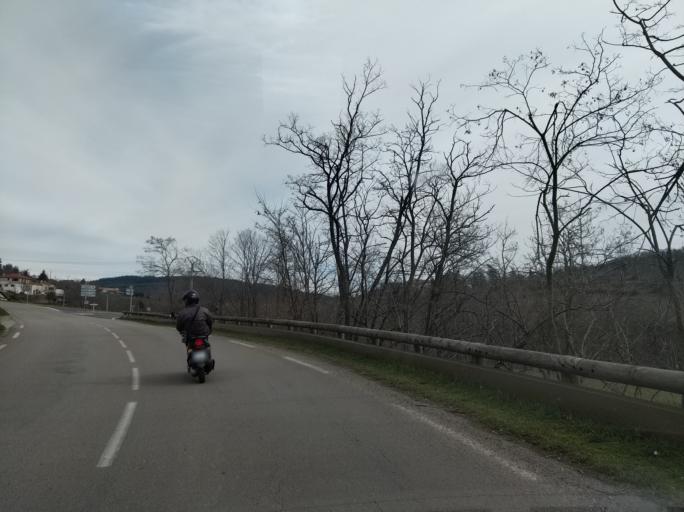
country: FR
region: Rhone-Alpes
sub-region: Departement de l'Ardeche
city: Satillieu
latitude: 45.1576
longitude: 4.6309
